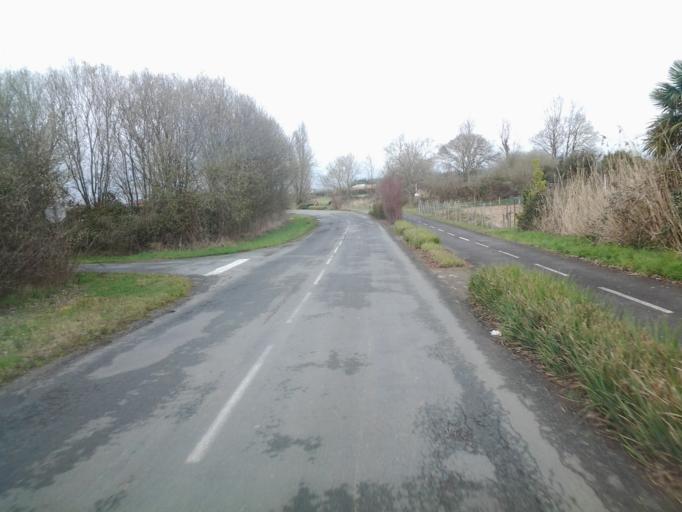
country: FR
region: Pays de la Loire
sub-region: Departement de la Vendee
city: La Tranche-sur-Mer
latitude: 46.3566
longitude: -1.4535
